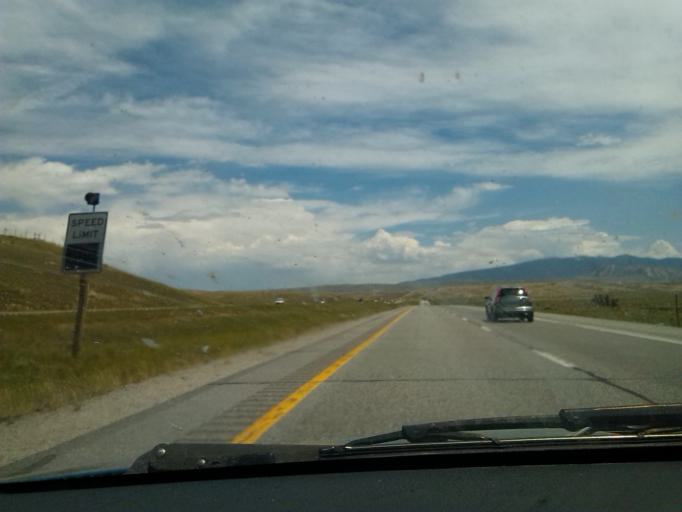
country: US
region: Wyoming
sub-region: Carbon County
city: Saratoga
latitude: 41.7408
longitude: -106.7620
